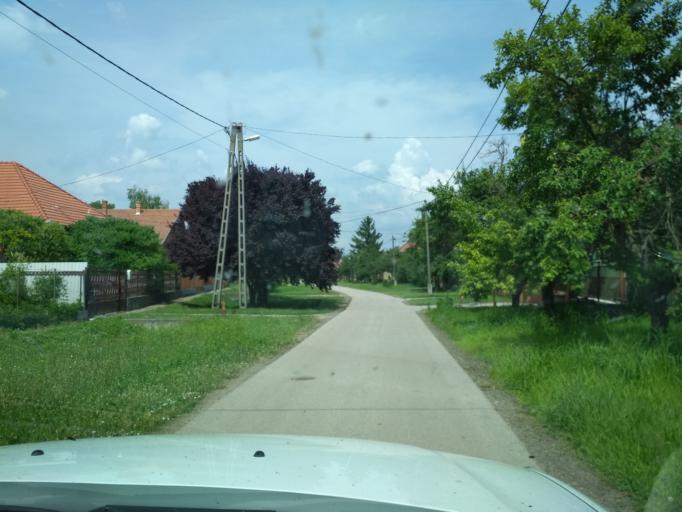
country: HU
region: Pest
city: Tapioszentmarton
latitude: 47.3381
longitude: 19.7408
